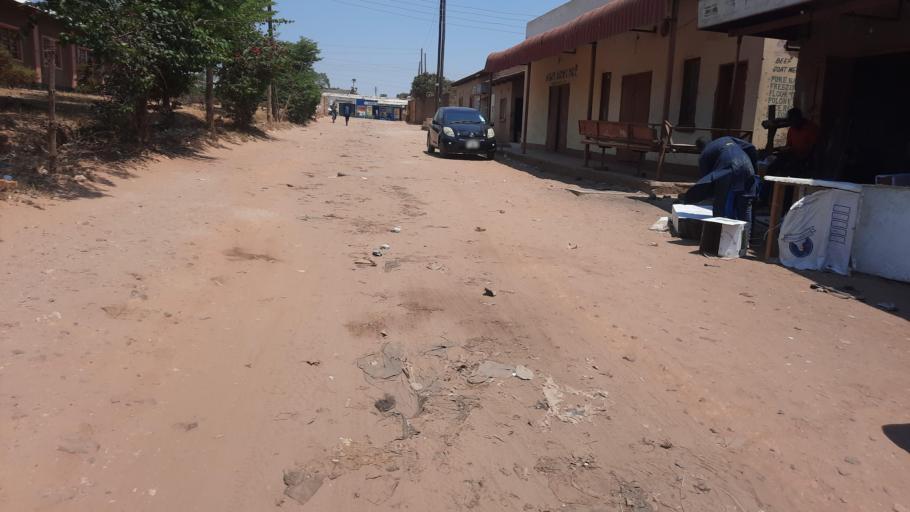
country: ZM
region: Lusaka
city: Lusaka
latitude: -15.4047
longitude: 28.3706
